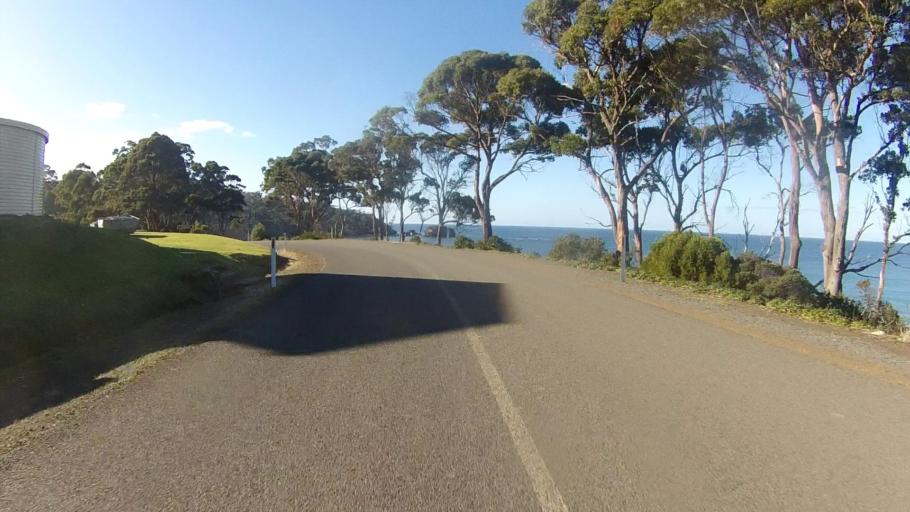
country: AU
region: Tasmania
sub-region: Sorell
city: Sorell
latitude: -43.0102
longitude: 147.9282
